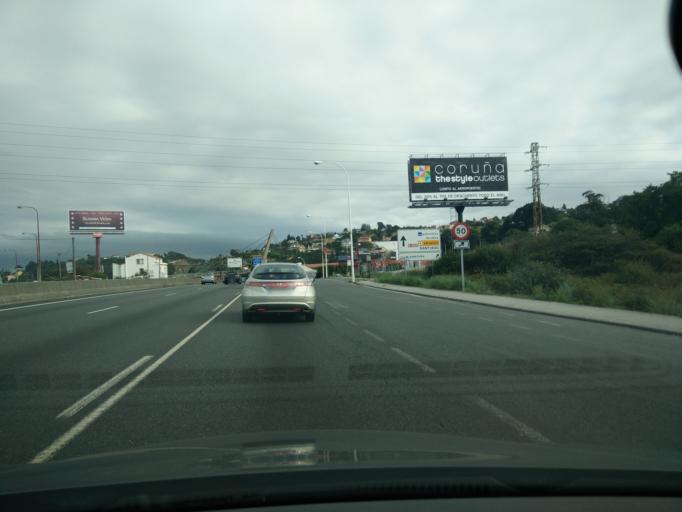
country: ES
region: Galicia
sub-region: Provincia da Coruna
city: A Coruna
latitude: 43.3332
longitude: -8.4018
